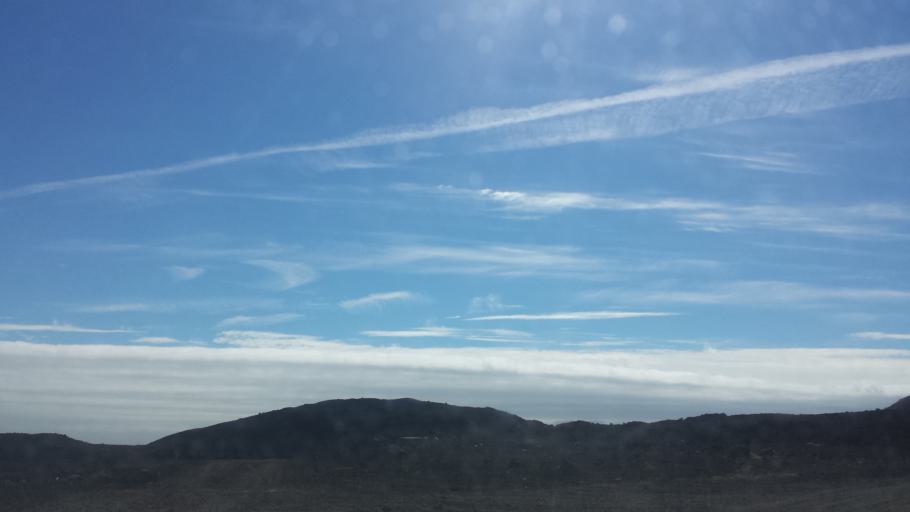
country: IS
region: South
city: Vestmannaeyjar
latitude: 63.4365
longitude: -20.2381
